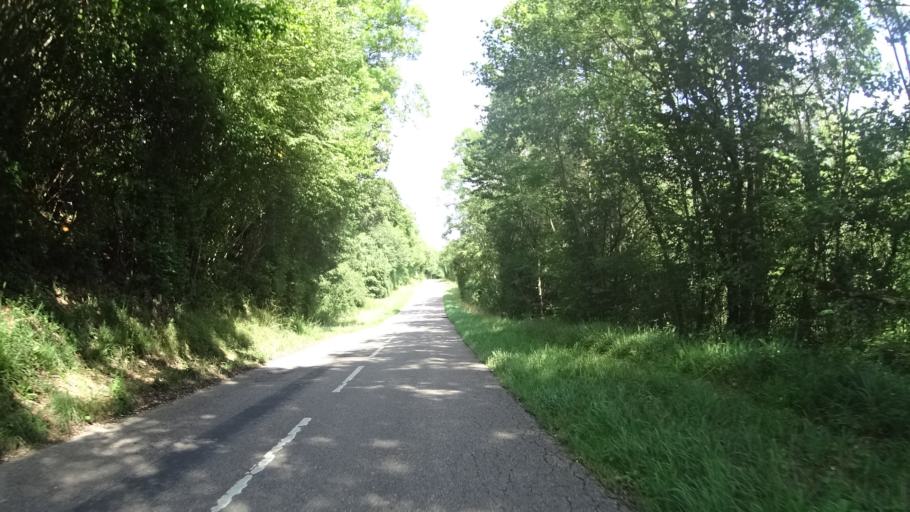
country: FR
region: Lorraine
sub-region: Departement de Meurthe-et-Moselle
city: Dommartin-les-Toul
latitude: 48.6472
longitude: 5.9263
